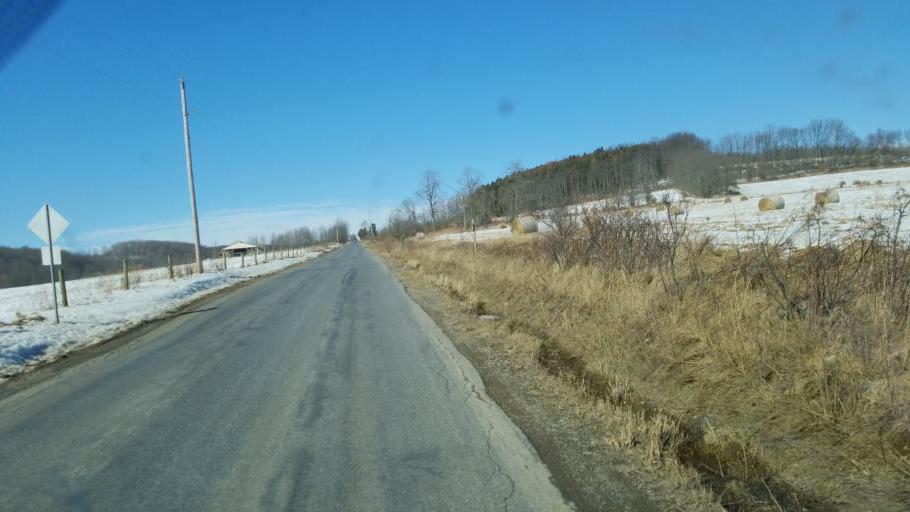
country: US
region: Pennsylvania
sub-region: Tioga County
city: Westfield
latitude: 41.9716
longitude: -77.6613
